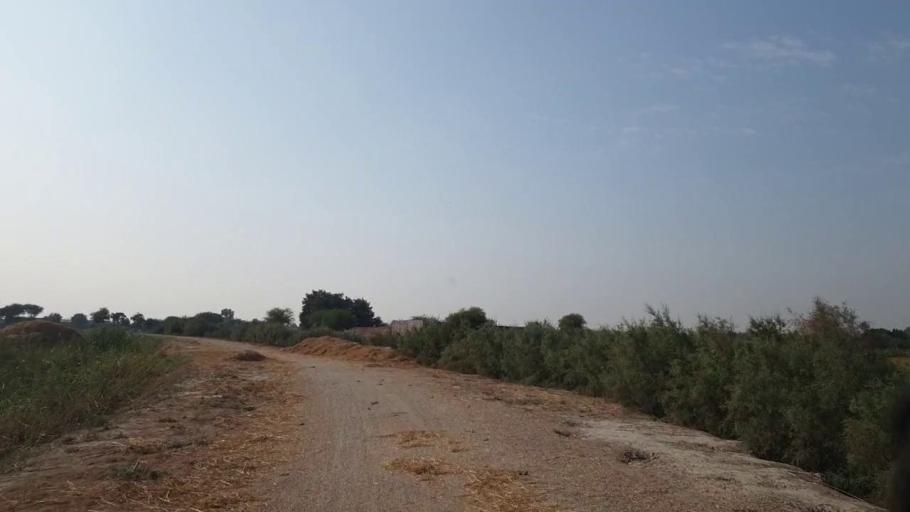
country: PK
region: Sindh
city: Tando Muhammad Khan
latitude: 25.0692
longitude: 68.4315
